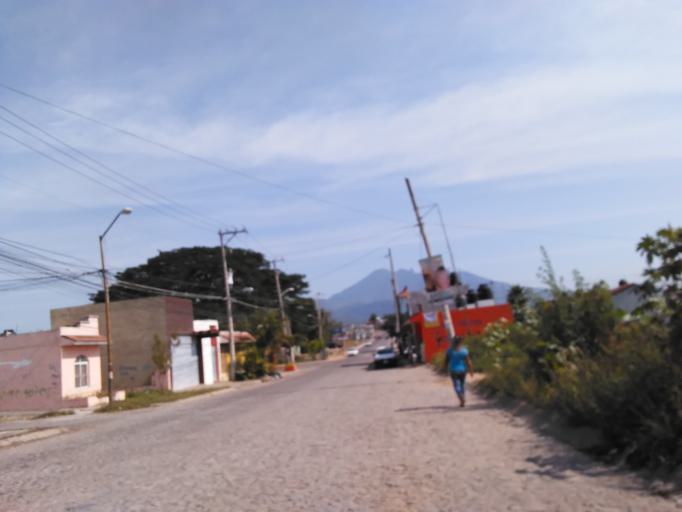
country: MX
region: Nayarit
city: Tepic
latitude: 21.4896
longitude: -104.8483
